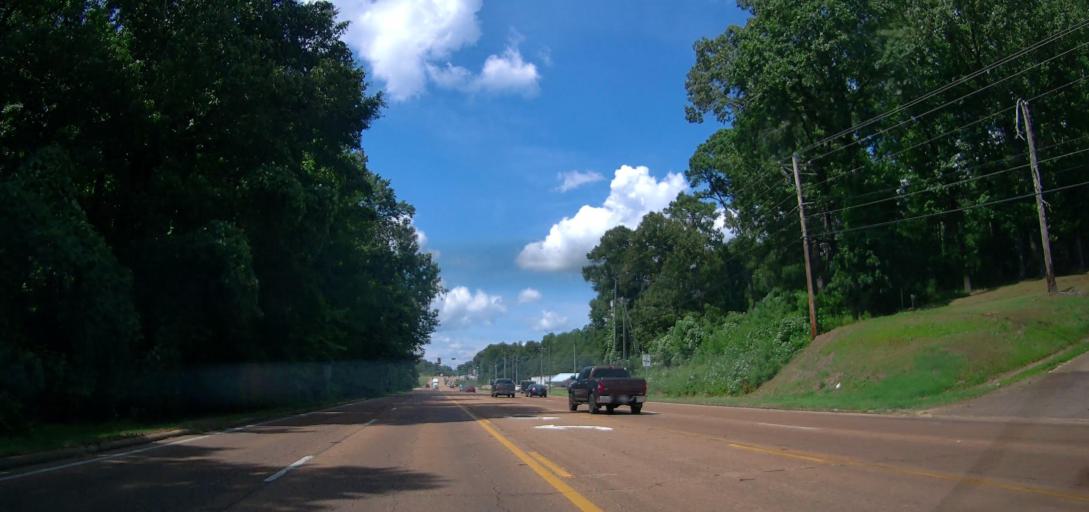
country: US
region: Mississippi
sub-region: Lowndes County
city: Columbus
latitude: 33.5556
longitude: -88.4331
